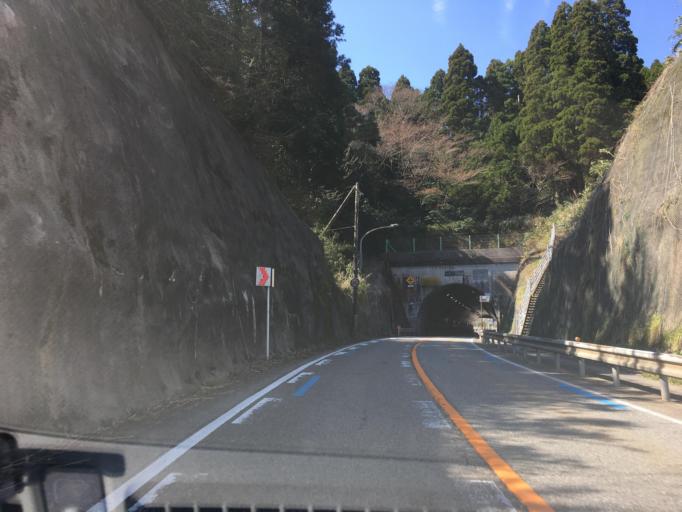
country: JP
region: Toyama
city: Himi
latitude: 36.8913
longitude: 137.0038
